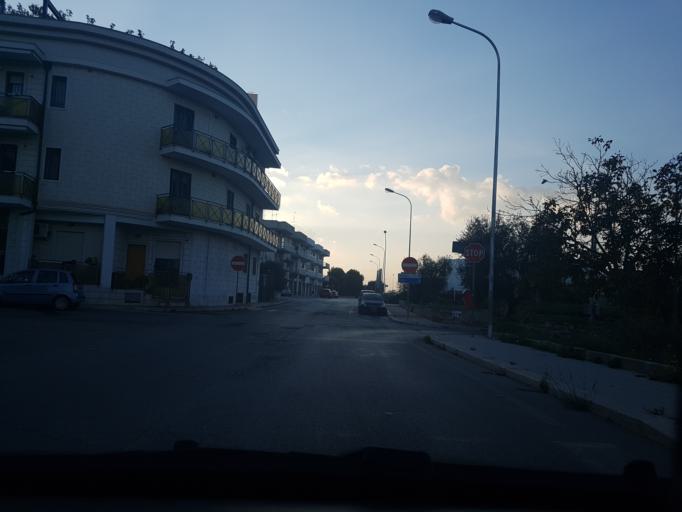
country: IT
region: Apulia
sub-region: Provincia di Bari
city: Bitritto
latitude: 41.0472
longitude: 16.8281
